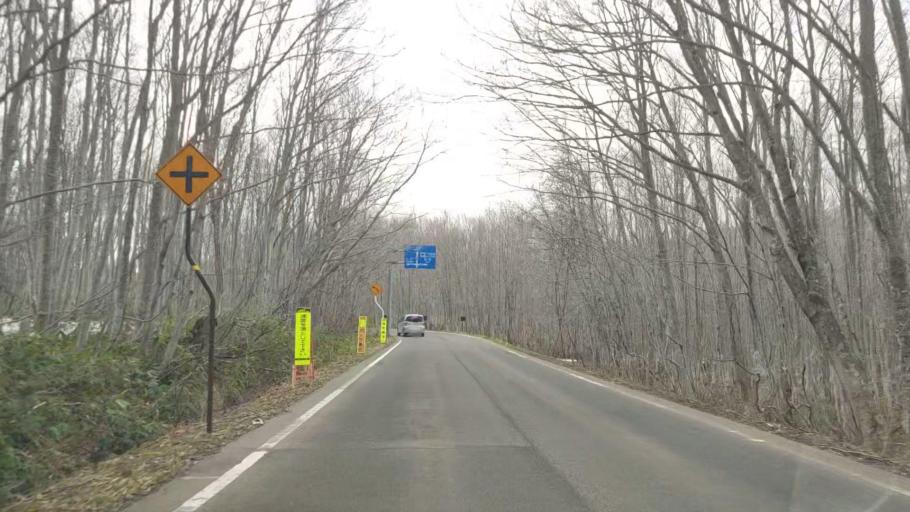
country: JP
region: Aomori
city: Aomori Shi
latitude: 40.6647
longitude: 140.9572
